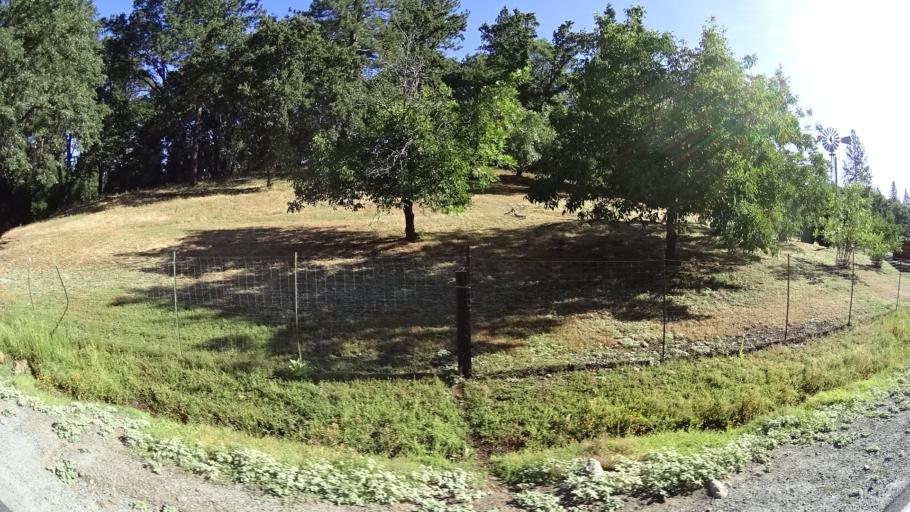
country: US
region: California
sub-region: Amador County
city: Pioneer
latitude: 38.4098
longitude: -120.5548
